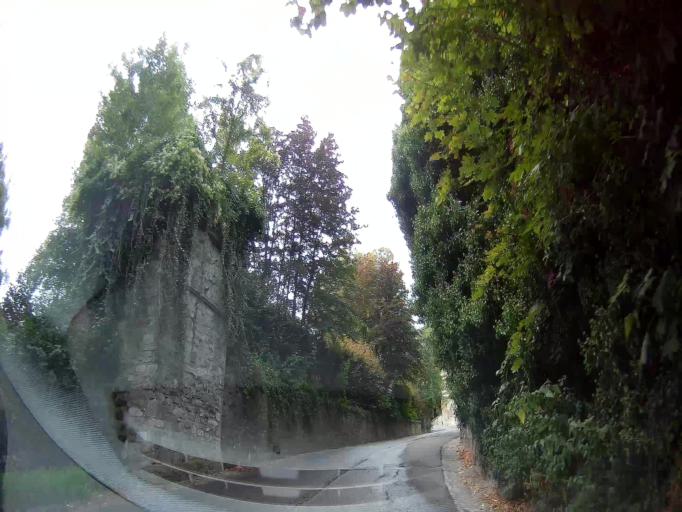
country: BE
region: Wallonia
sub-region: Province de Liege
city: Limbourg
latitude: 50.6139
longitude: 5.9410
